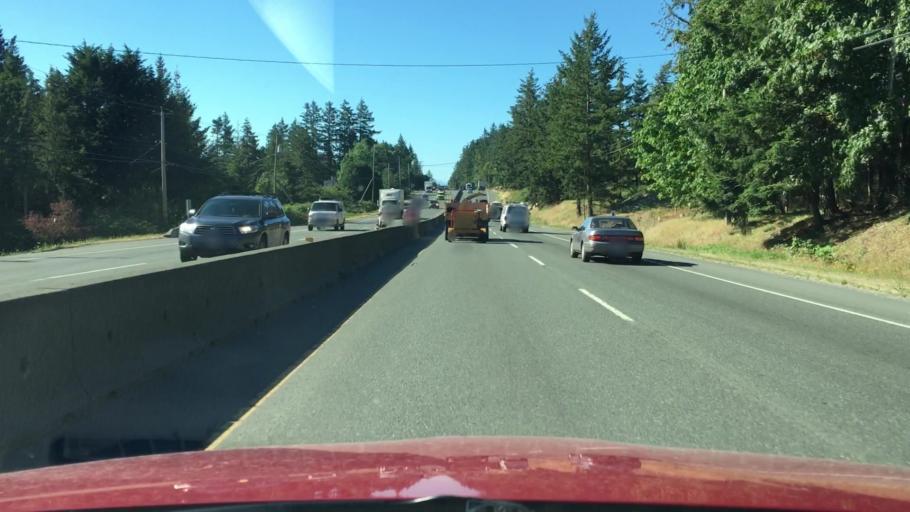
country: CA
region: British Columbia
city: Victoria
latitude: 48.5490
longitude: -123.3919
